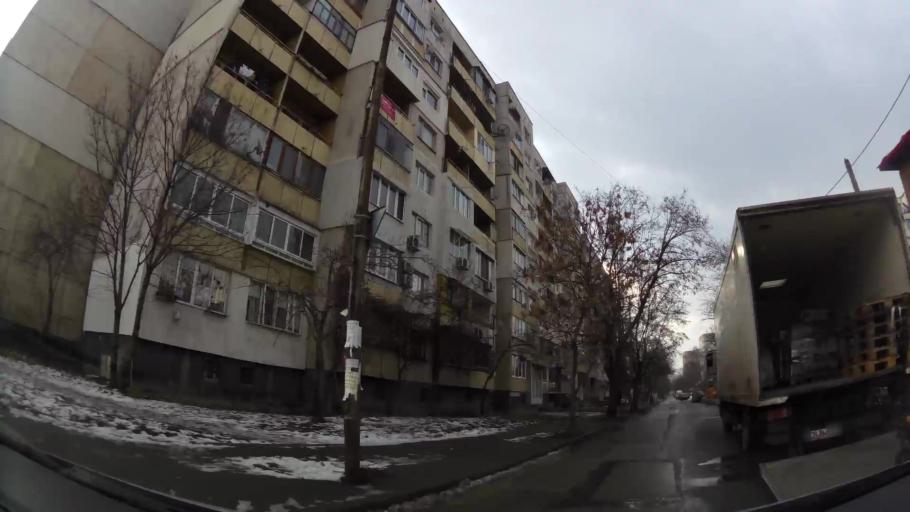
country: BG
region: Sofia-Capital
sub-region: Stolichna Obshtina
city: Sofia
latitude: 42.6983
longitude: 23.2893
